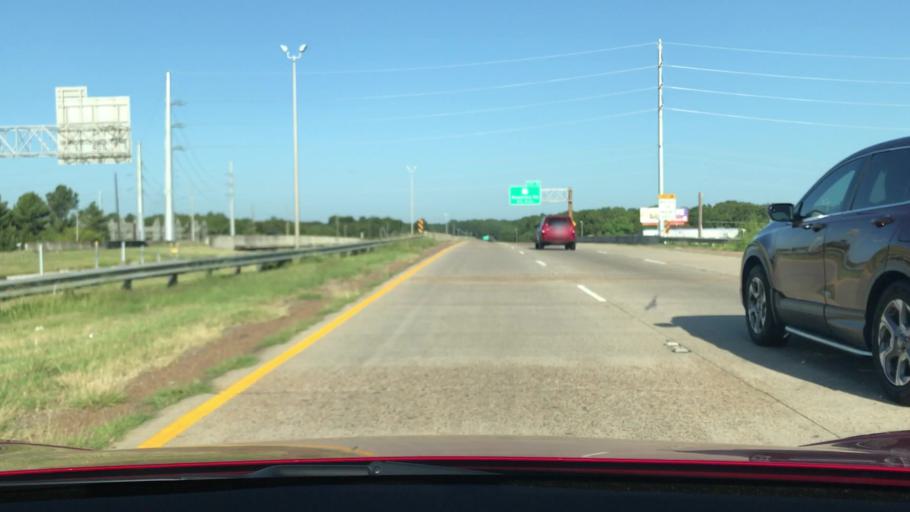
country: US
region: Louisiana
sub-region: Bossier Parish
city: Bossier City
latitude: 32.4207
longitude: -93.7621
